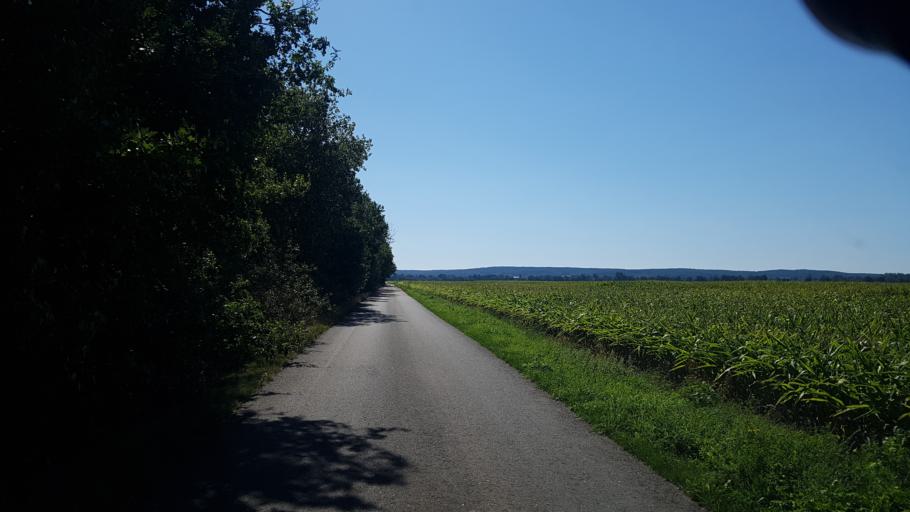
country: DE
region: Brandenburg
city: Plessa
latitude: 51.4352
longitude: 13.6069
